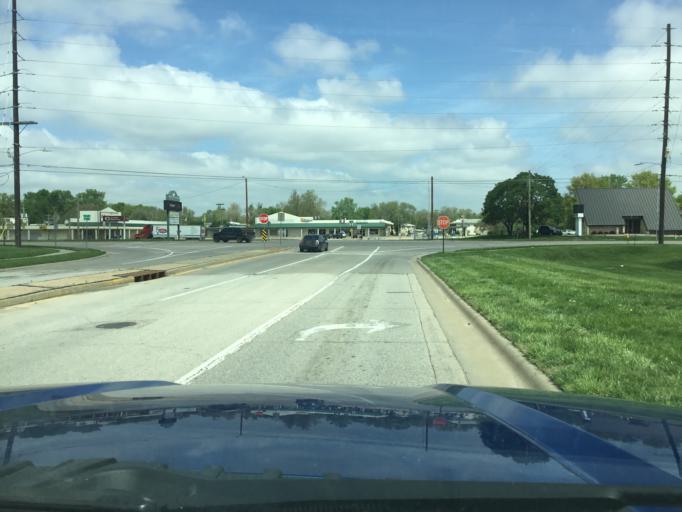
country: US
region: Kansas
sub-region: Shawnee County
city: Topeka
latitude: 39.0436
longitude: -95.6350
